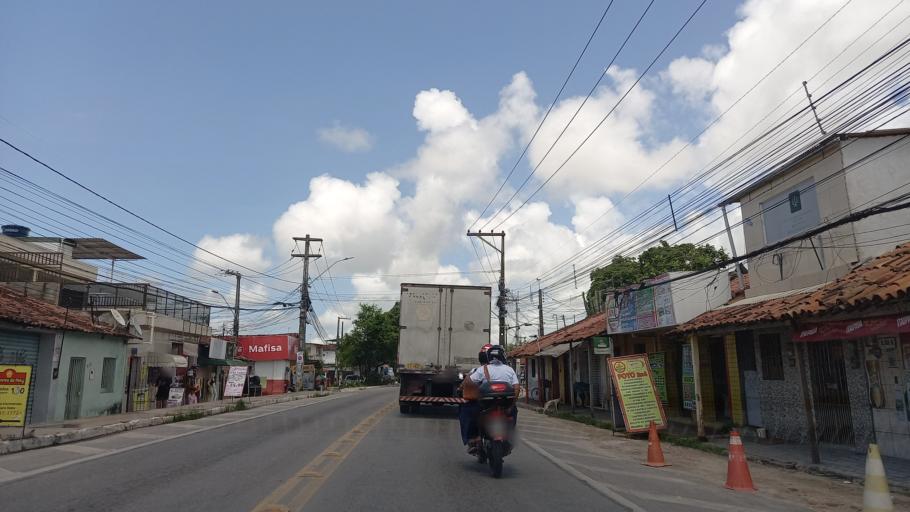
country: BR
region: Pernambuco
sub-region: Jaboatao Dos Guararapes
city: Jaboatao
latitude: -8.2233
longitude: -34.9665
